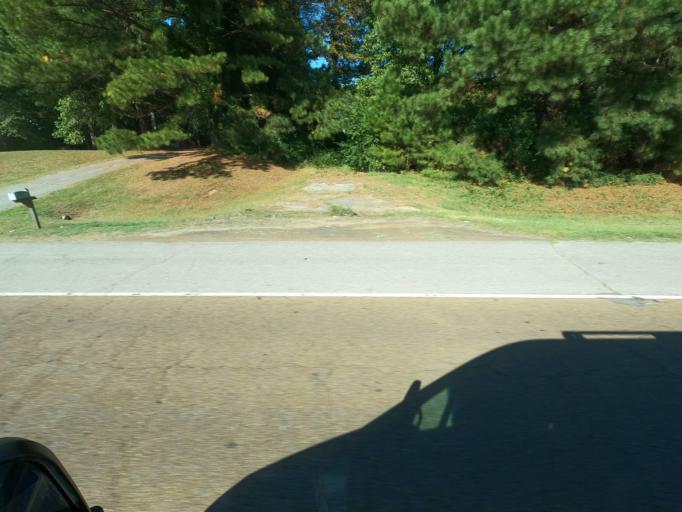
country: US
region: Tennessee
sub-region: Shelby County
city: Millington
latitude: 35.3905
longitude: -89.8557
